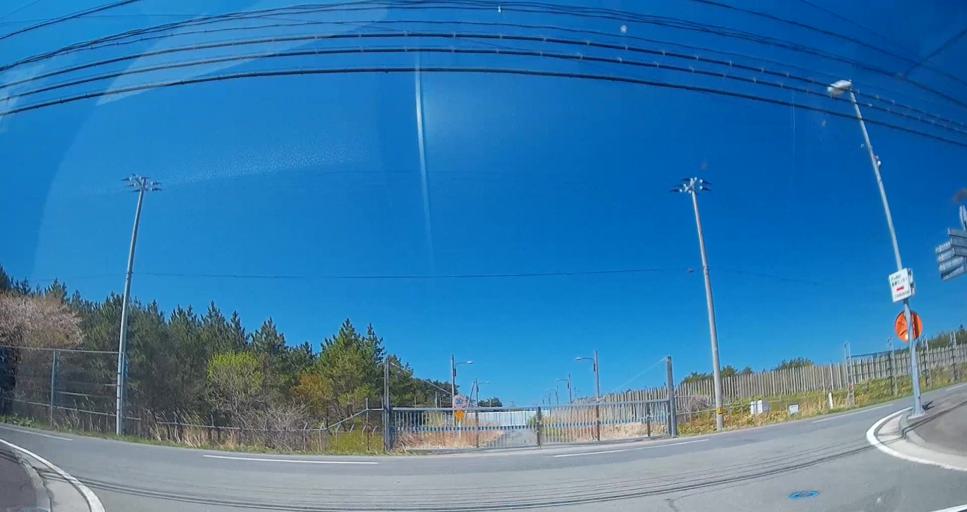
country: JP
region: Aomori
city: Misawa
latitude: 40.9702
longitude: 141.3596
